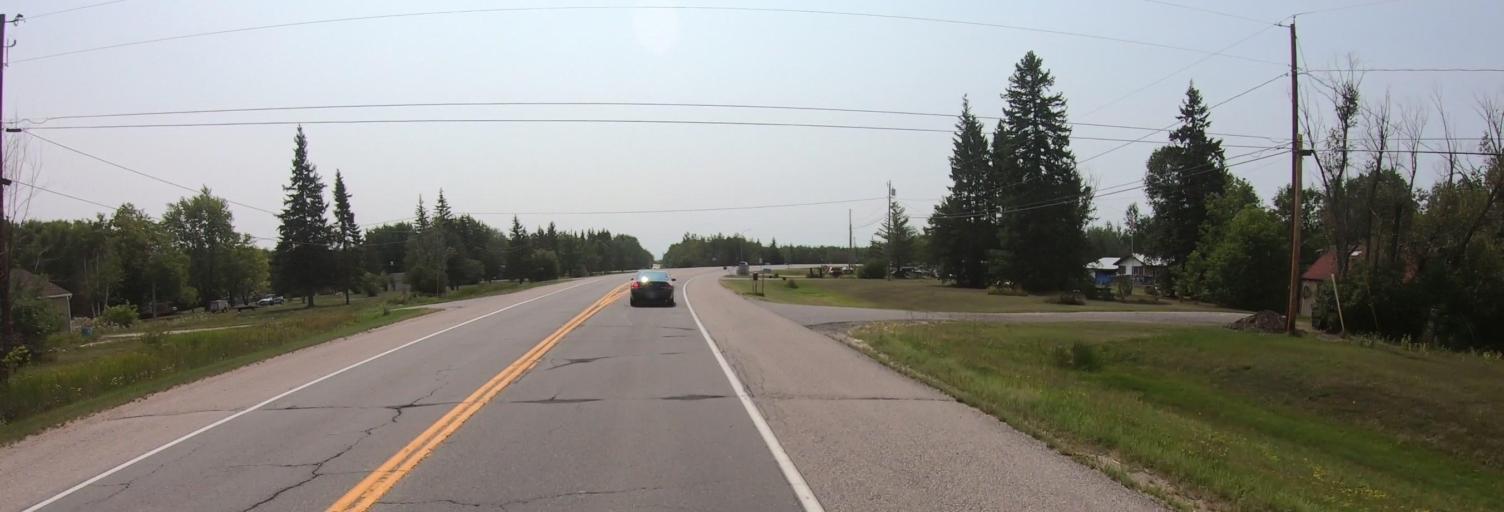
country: US
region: Minnesota
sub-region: Koochiching County
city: International Falls
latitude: 48.5579
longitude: -93.4402
